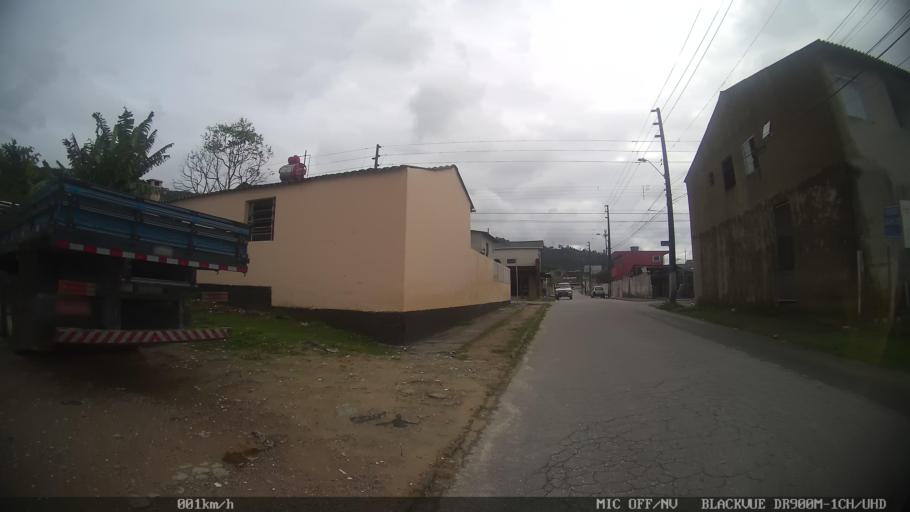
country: BR
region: Santa Catarina
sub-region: Biguacu
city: Biguacu
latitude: -27.5432
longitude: -48.6456
